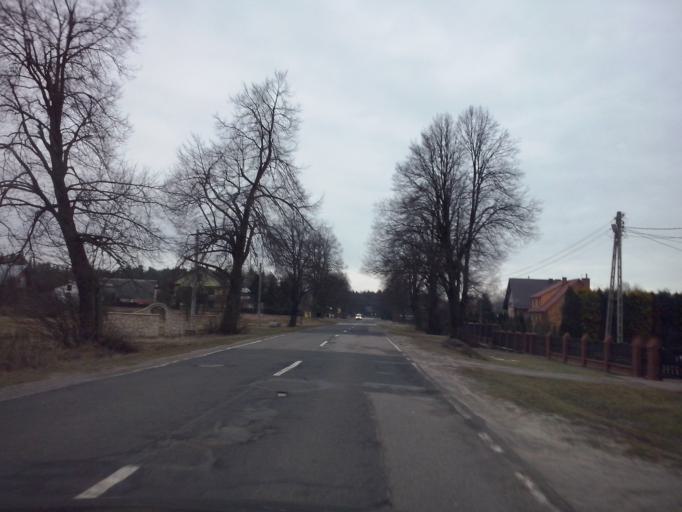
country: PL
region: Subcarpathian Voivodeship
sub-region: Powiat nizanski
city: Harasiuki
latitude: 50.4807
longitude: 22.4758
